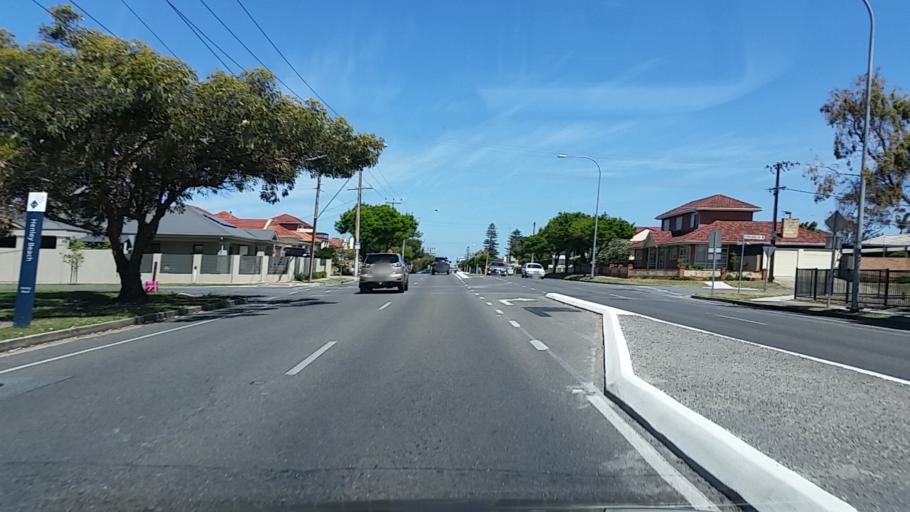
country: AU
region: South Australia
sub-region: Charles Sturt
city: Grange
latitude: -34.9072
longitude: 138.4985
